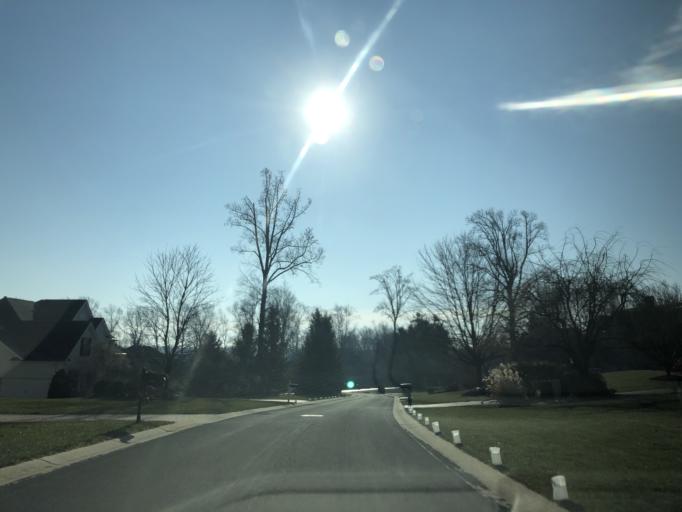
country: US
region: Pennsylvania
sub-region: Chester County
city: Downingtown
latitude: 39.9906
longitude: -75.7077
